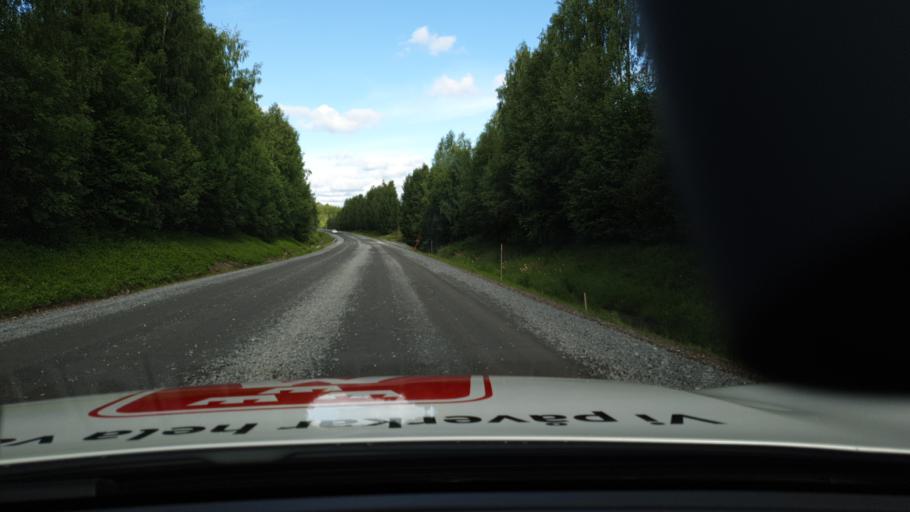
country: SE
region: Norrbotten
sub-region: Bodens Kommun
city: Boden
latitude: 65.8488
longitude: 21.5865
